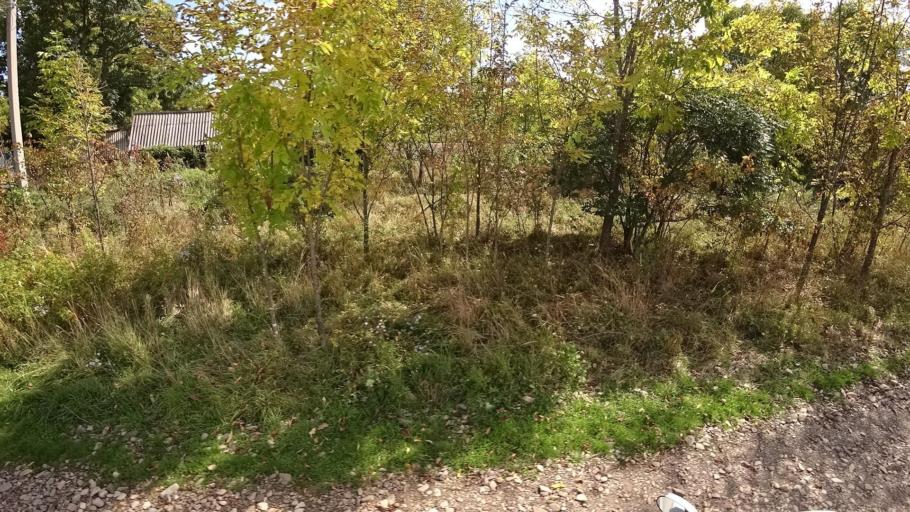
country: RU
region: Primorskiy
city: Kirovskiy
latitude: 44.7549
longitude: 133.6110
